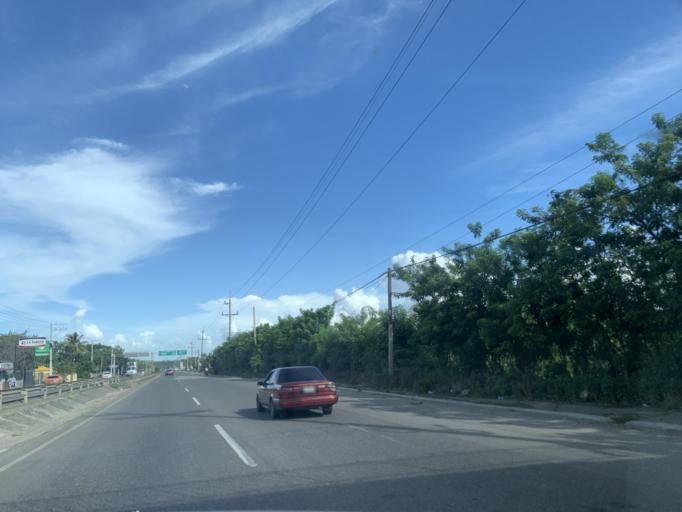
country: DO
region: Santiago
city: Villa Gonzalez
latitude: 19.5324
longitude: -70.7800
